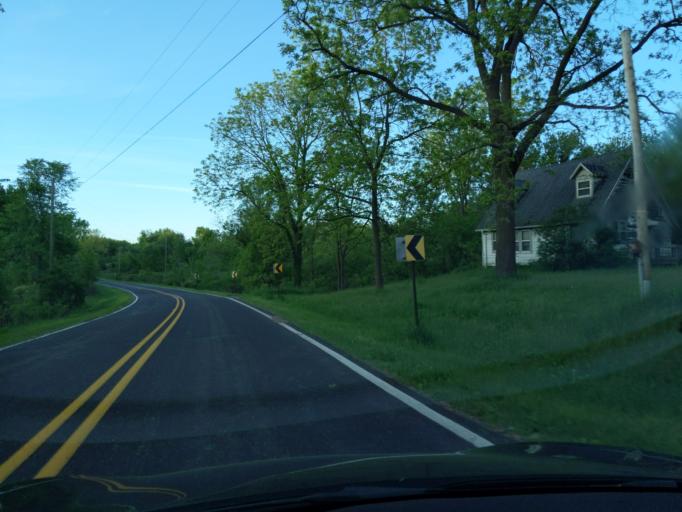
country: US
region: Michigan
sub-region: Ingham County
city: Leslie
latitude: 42.4971
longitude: -84.3152
